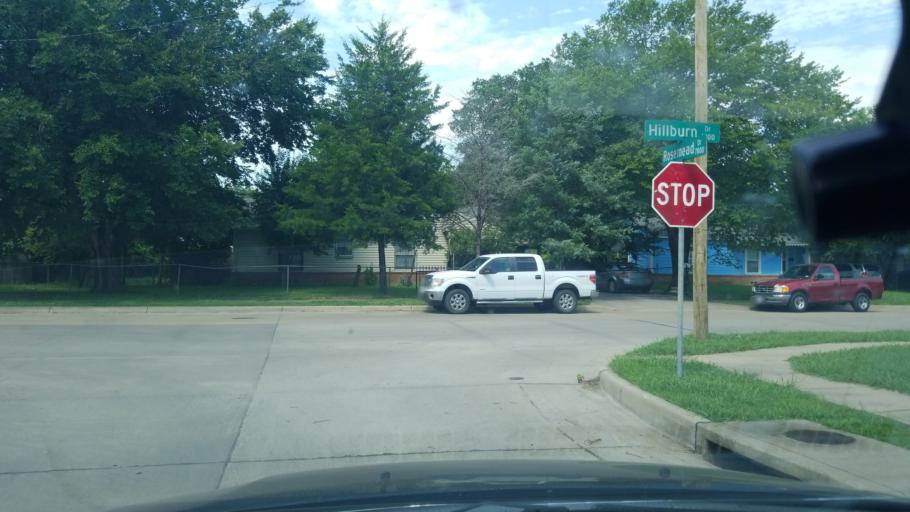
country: US
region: Texas
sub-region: Dallas County
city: Balch Springs
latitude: 32.7369
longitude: -96.6884
